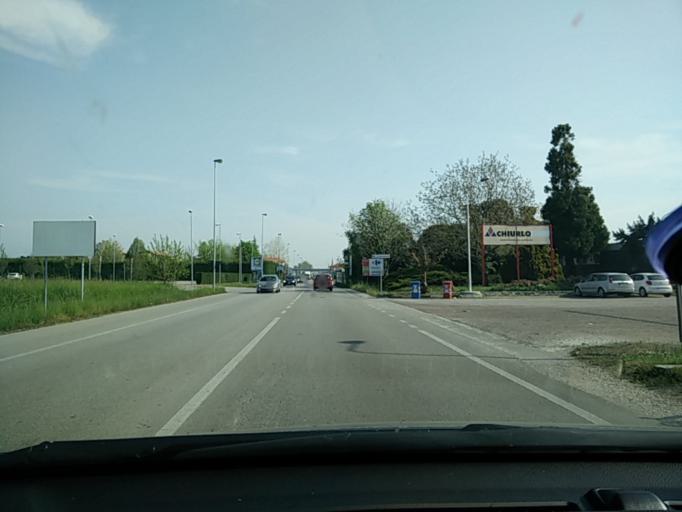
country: IT
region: Friuli Venezia Giulia
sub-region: Provincia di Pordenone
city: Pordenone
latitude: 45.9391
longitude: 12.6506
